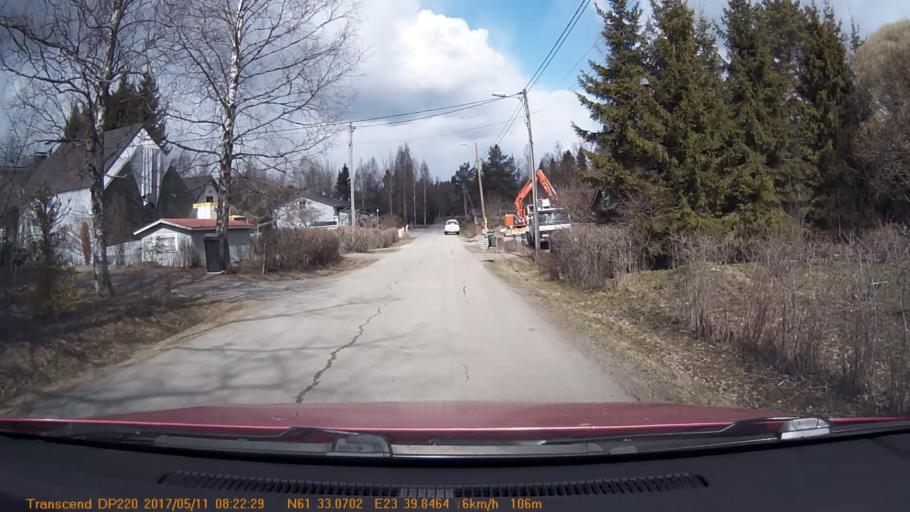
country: FI
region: Pirkanmaa
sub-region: Tampere
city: Yloejaervi
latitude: 61.5511
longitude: 23.6642
